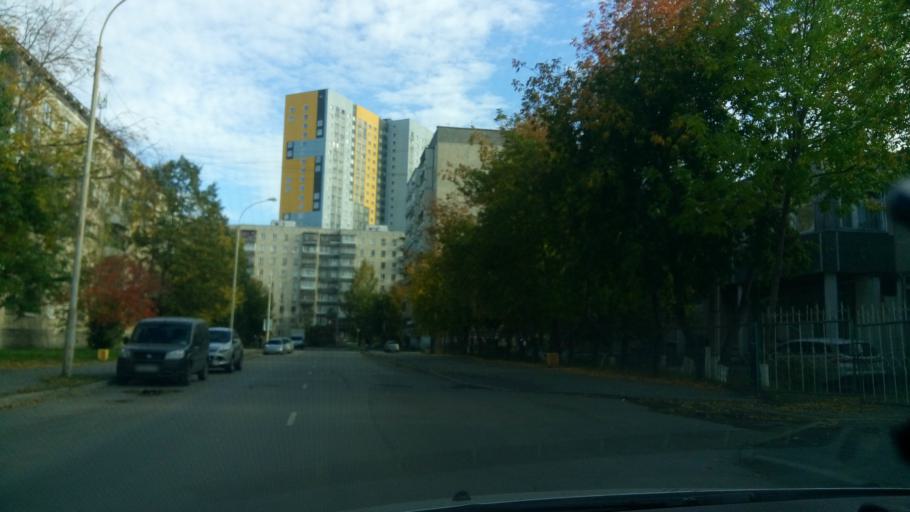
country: RU
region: Sverdlovsk
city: Yekaterinburg
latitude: 56.9054
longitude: 60.6033
